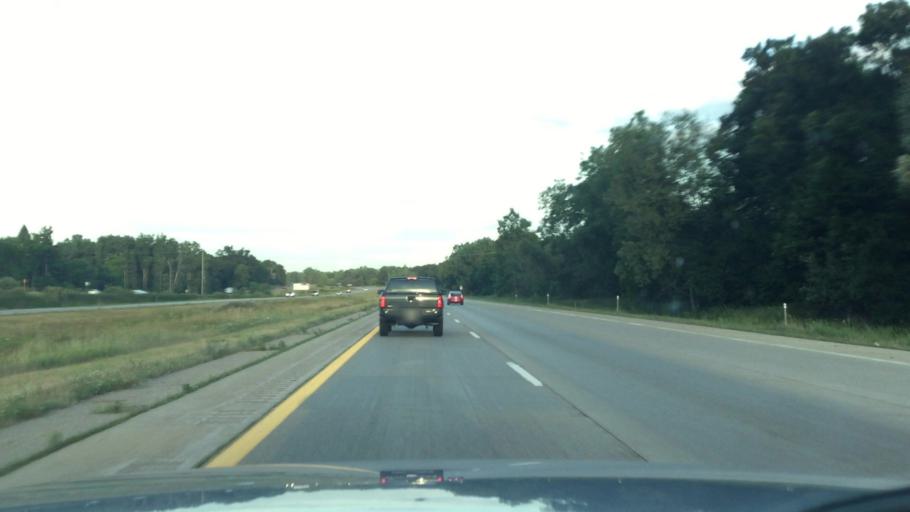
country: US
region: Michigan
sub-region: Ingham County
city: Haslett
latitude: 42.7988
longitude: -84.3542
